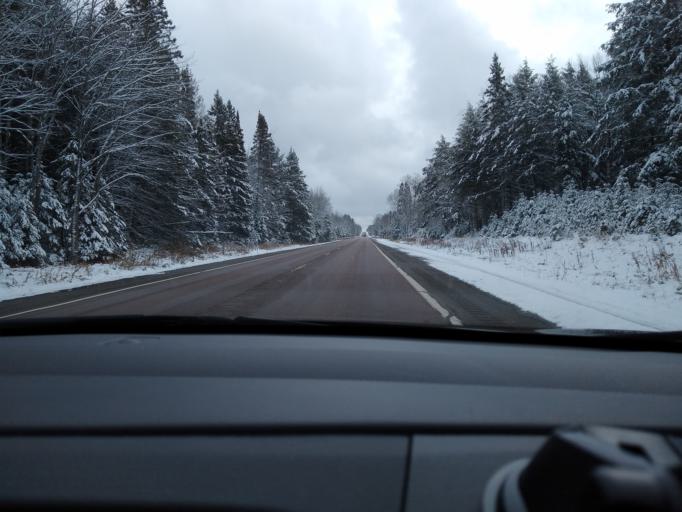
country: US
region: Wisconsin
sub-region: Vilas County
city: Eagle River
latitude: 46.2135
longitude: -89.0407
